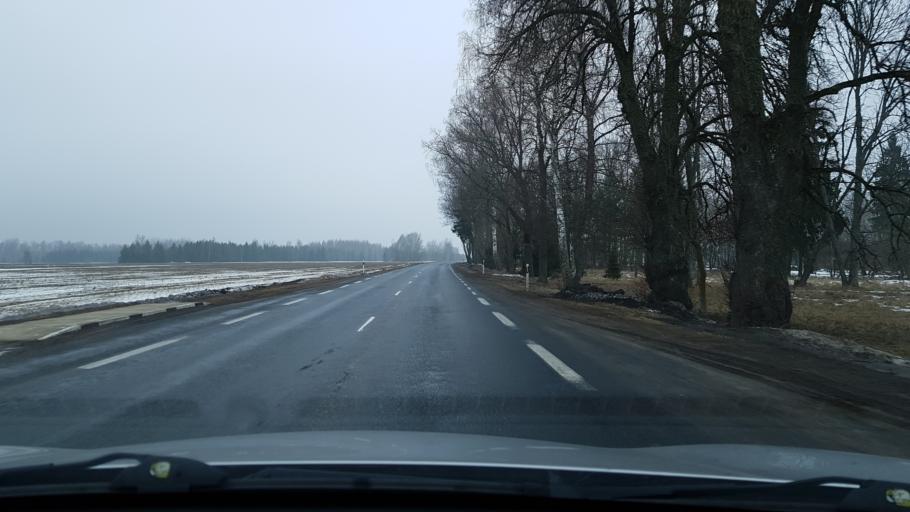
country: EE
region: Valgamaa
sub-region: Torva linn
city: Torva
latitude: 58.1833
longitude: 25.9533
